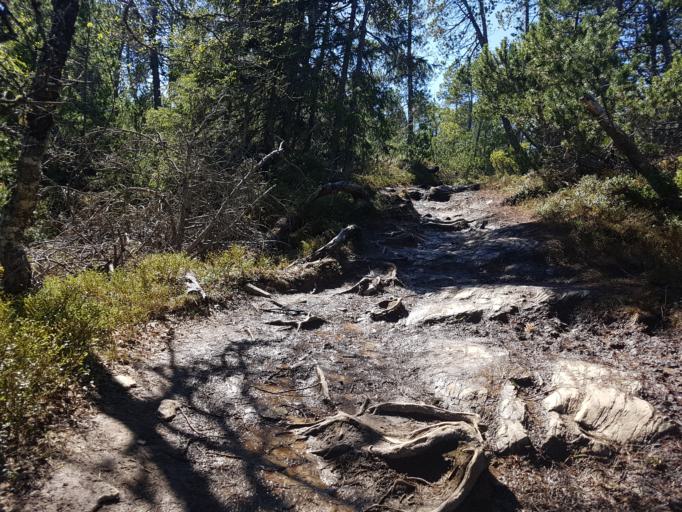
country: NO
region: Sor-Trondelag
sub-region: Trondheim
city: Trondheim
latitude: 63.4329
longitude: 10.3104
